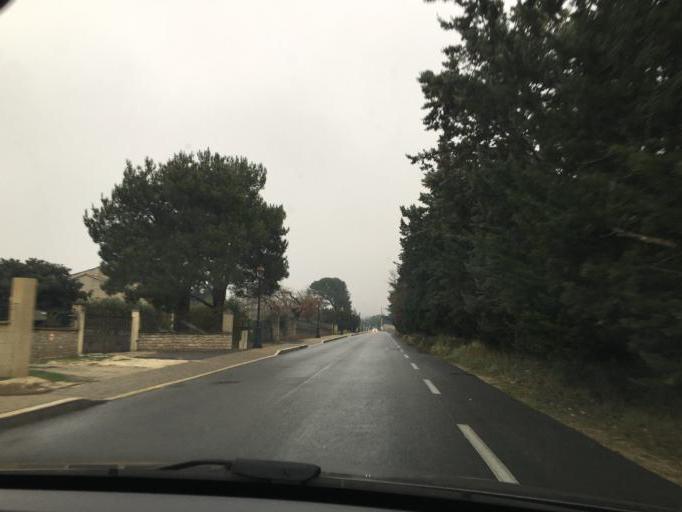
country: FR
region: Provence-Alpes-Cote d'Azur
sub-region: Departement du Vaucluse
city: Gordes
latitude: 43.8853
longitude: 5.1713
